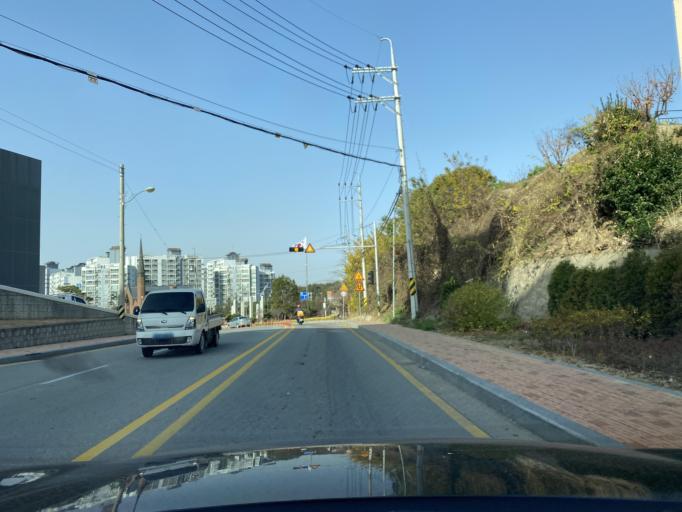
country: KR
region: Chungcheongnam-do
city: Yesan
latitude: 36.6864
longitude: 126.8445
